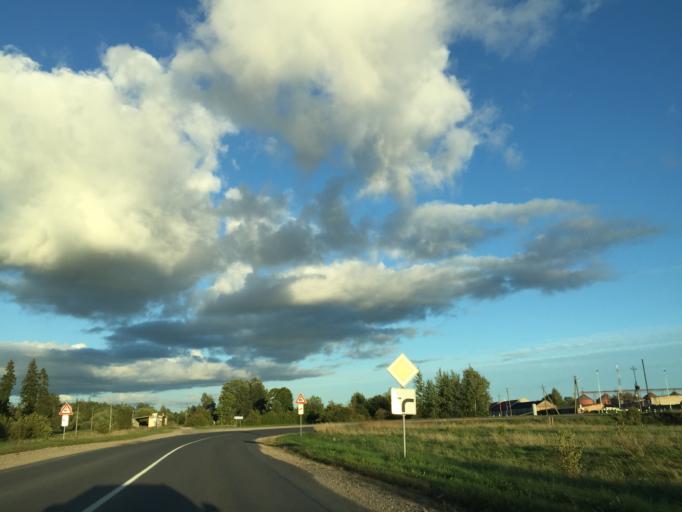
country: LV
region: Saldus Rajons
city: Saldus
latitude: 56.6889
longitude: 22.4573
